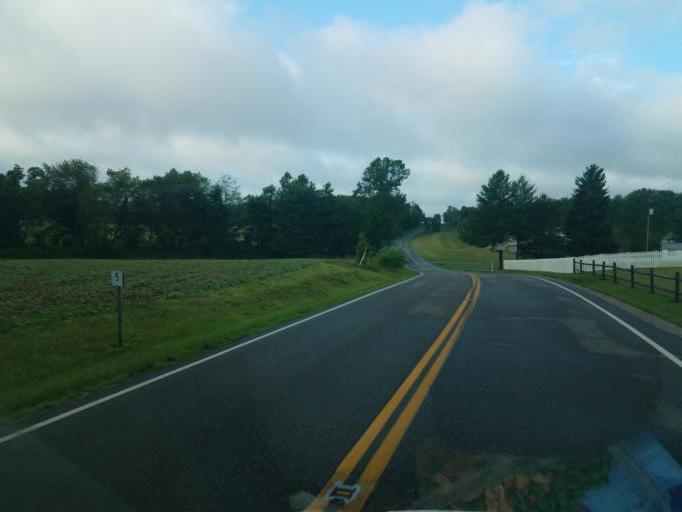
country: US
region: Ohio
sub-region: Gallia County
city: Gallipolis
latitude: 38.8631
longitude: -82.3847
